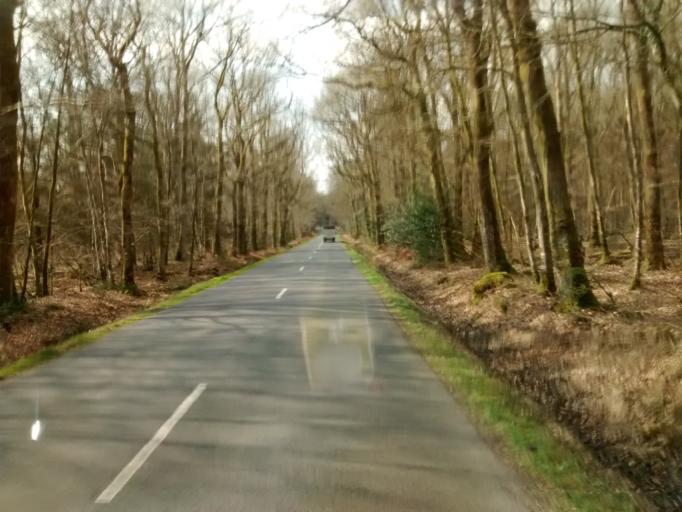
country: FR
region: Brittany
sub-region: Departement d'Ille-et-Vilaine
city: Plelan-le-Grand
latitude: 48.0120
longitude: -2.1334
